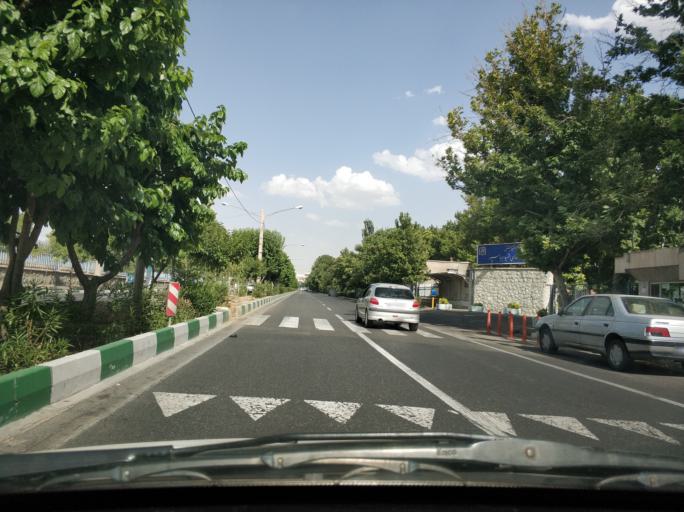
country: IR
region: Tehran
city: Tajrish
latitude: 35.7443
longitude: 51.5785
